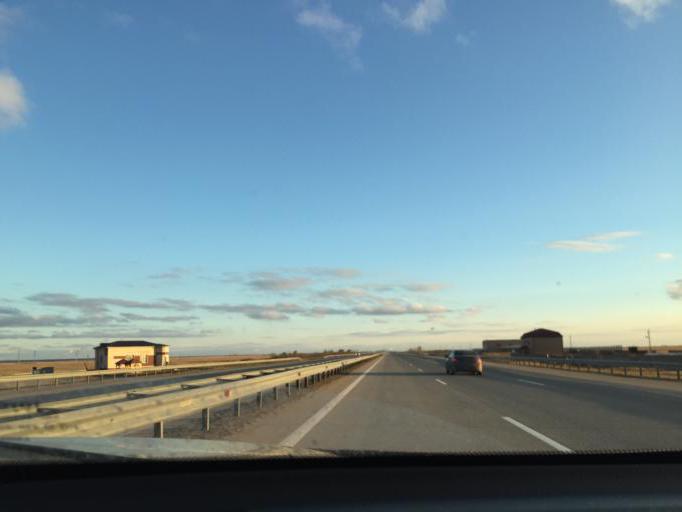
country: KZ
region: Astana Qalasy
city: Astana
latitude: 51.2914
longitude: 71.3591
